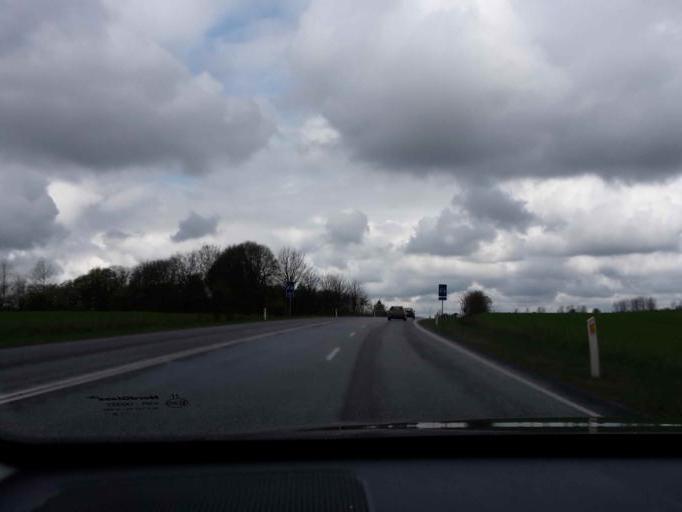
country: DK
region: South Denmark
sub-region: Vejle Kommune
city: Jelling
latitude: 55.6952
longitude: 9.3864
